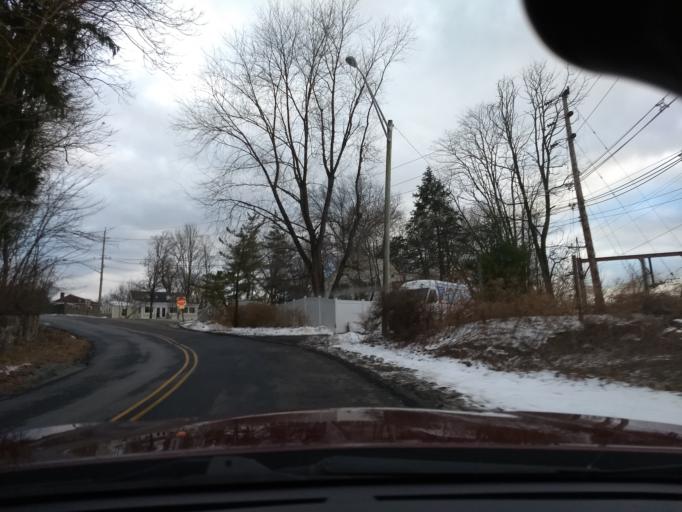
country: US
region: New Jersey
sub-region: Morris County
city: Morris Plains
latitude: 40.8113
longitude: -74.4774
